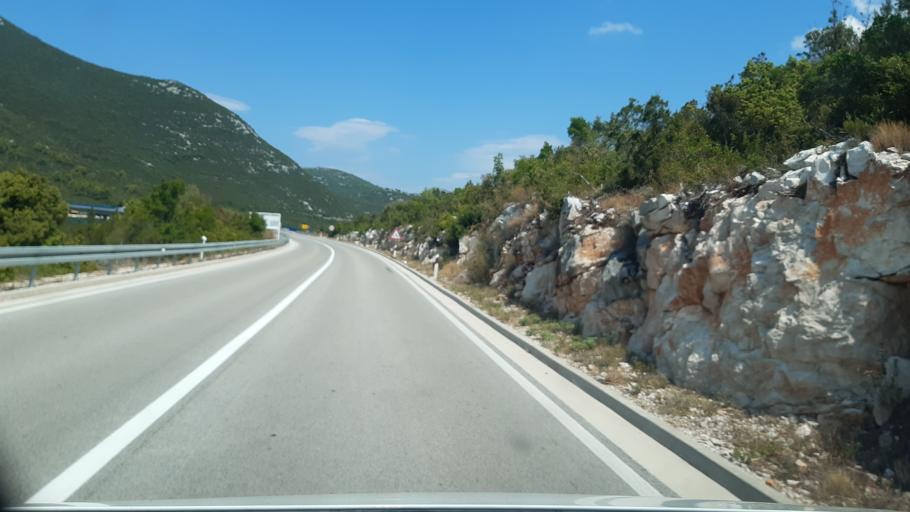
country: HR
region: Dubrovacko-Neretvanska
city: Ston
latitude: 42.8652
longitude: 17.7026
